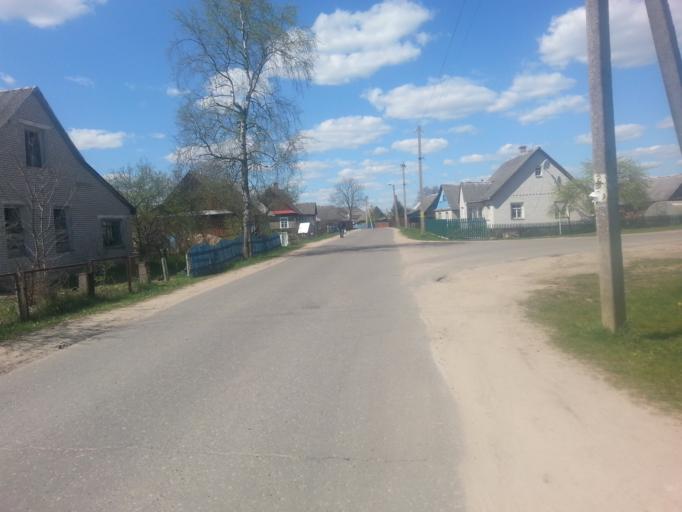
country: BY
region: Minsk
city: Narach
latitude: 54.9316
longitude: 26.6888
